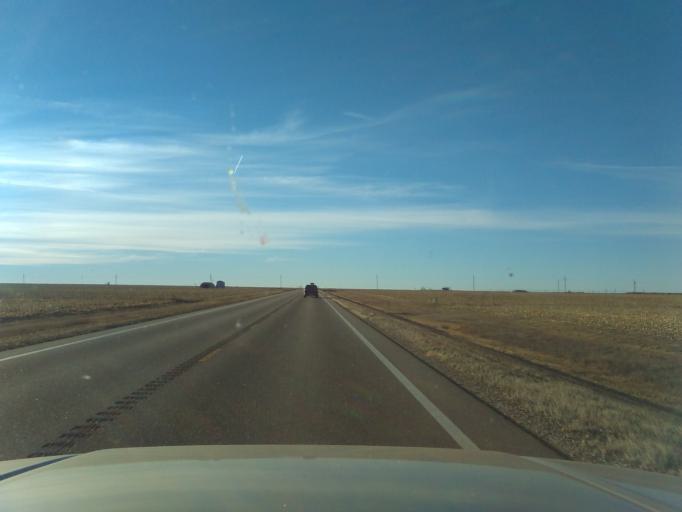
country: US
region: Kansas
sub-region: Thomas County
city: Colby
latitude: 39.4649
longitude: -100.7520
